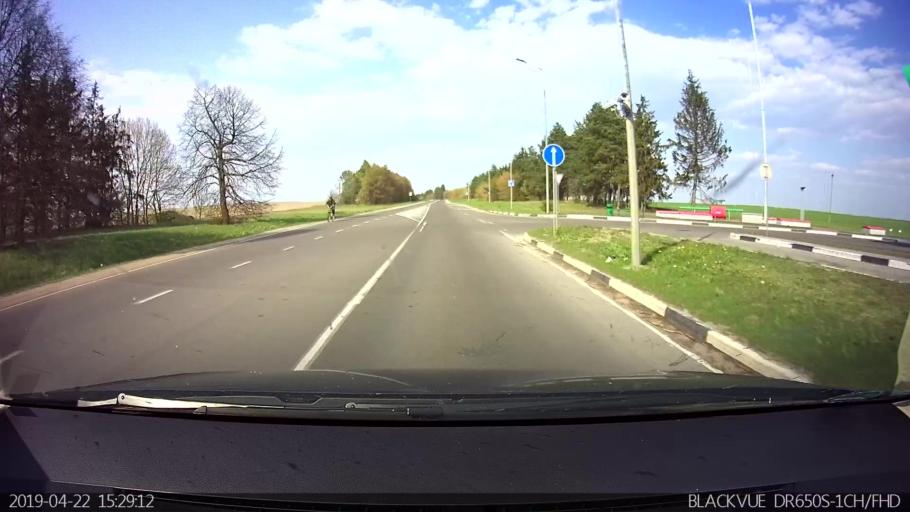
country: BY
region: Brest
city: Vysokaye
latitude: 52.3825
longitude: 23.3716
